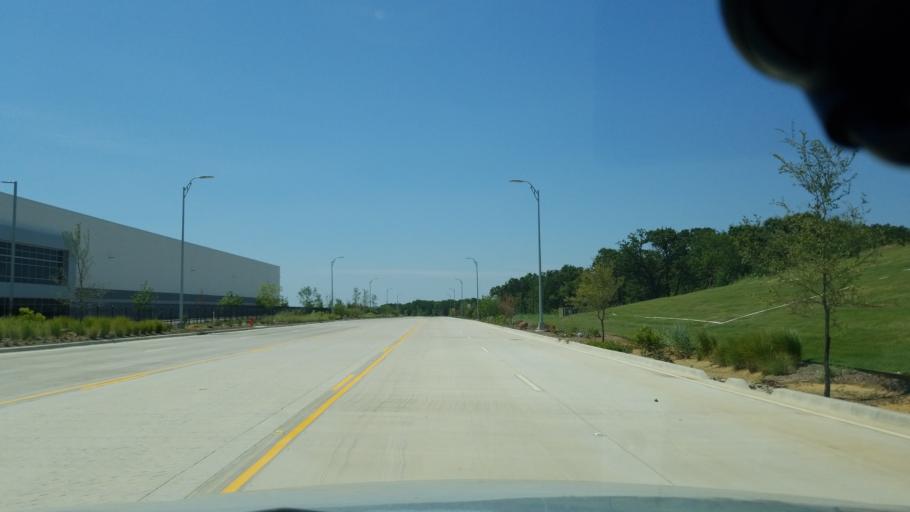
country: US
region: Texas
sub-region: Tarrant County
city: Euless
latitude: 32.8450
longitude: -97.0310
